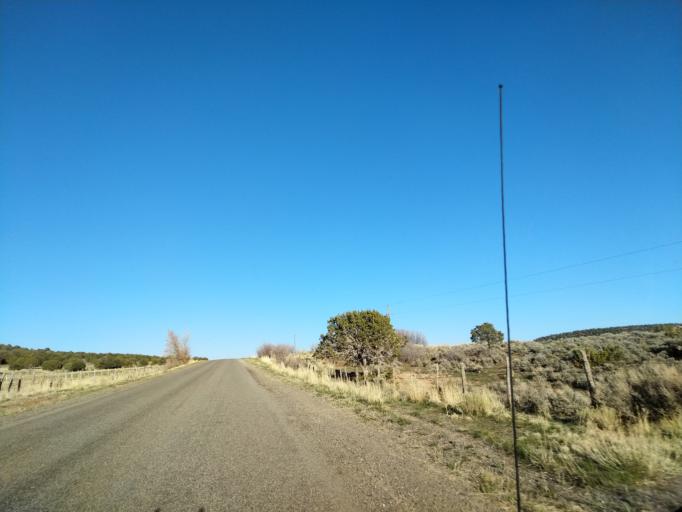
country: US
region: Colorado
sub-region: Mesa County
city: Loma
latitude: 38.9487
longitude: -108.9723
